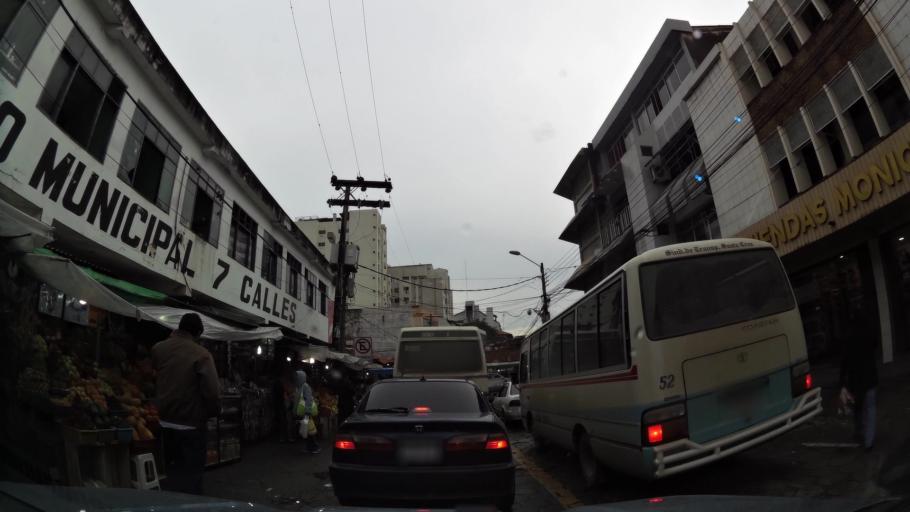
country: BO
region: Santa Cruz
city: Santa Cruz de la Sierra
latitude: -17.7865
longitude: -63.1856
